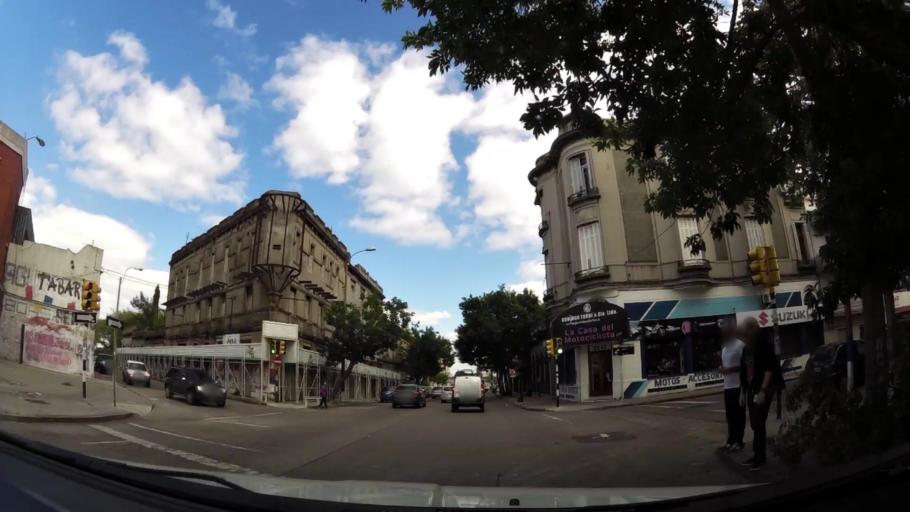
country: UY
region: Montevideo
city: Montevideo
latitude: -34.8927
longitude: -56.1851
